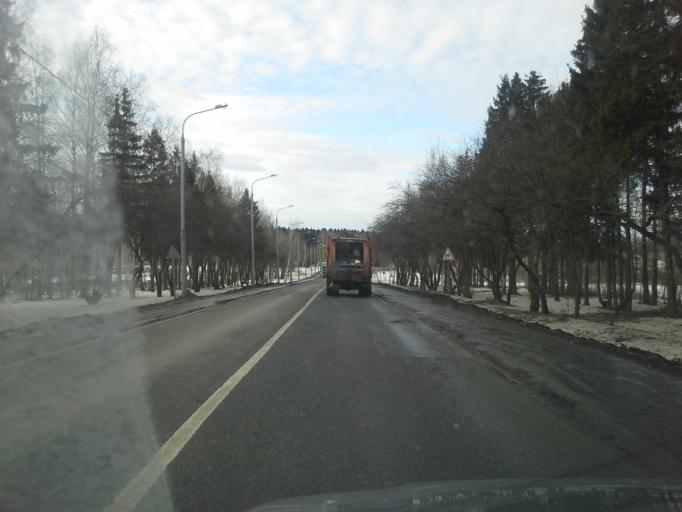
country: RU
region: Moskovskaya
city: Kokoshkino
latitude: 55.5661
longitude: 37.1507
